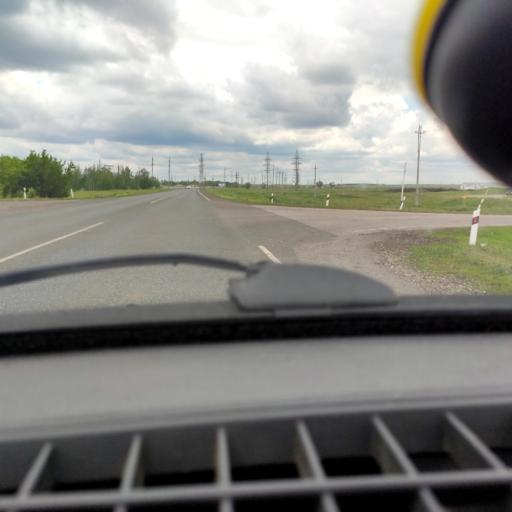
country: RU
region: Samara
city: Povolzhskiy
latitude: 53.6530
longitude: 49.6910
